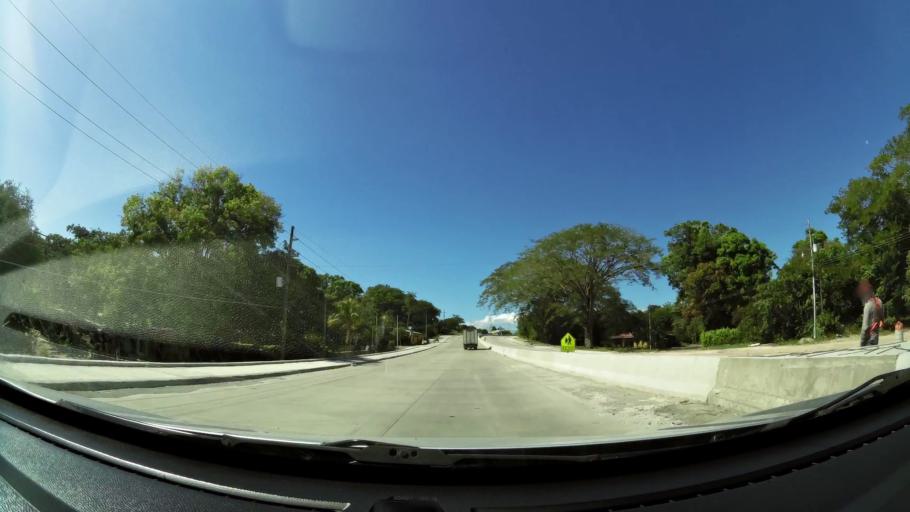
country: CR
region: Guanacaste
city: Liberia
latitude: 10.5654
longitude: -85.3885
